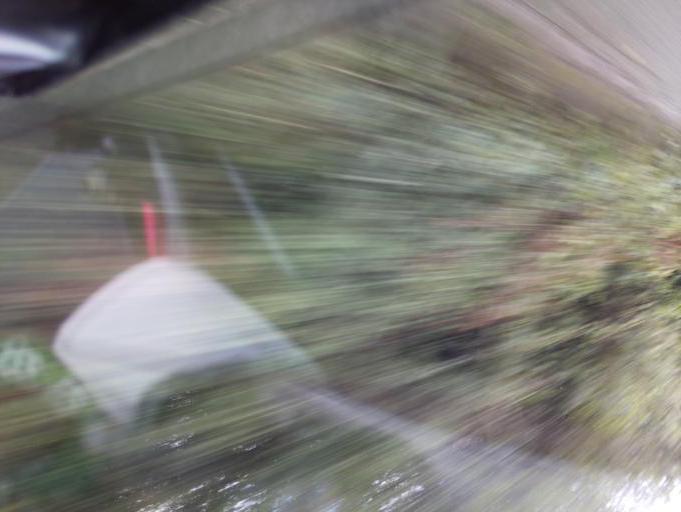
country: GB
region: England
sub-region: Devon
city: Modbury
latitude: 50.3377
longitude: -3.8568
